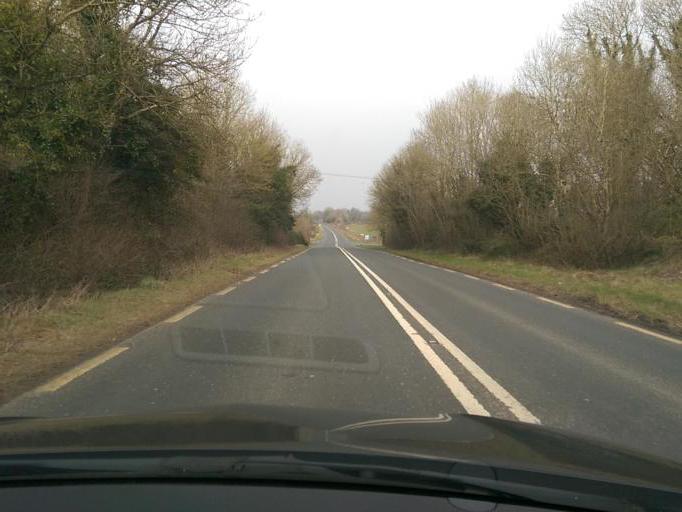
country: IE
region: Connaught
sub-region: Roscommon
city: Roscommon
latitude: 53.6478
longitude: -8.1286
